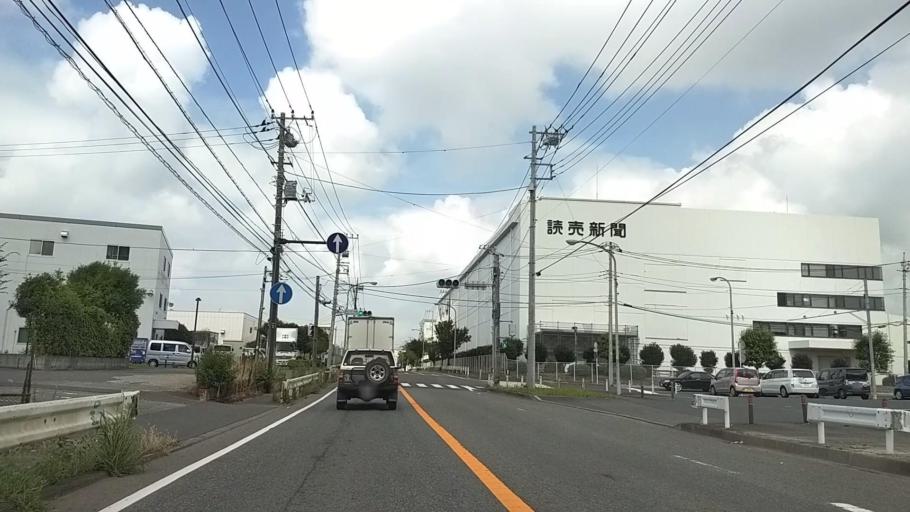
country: JP
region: Kanagawa
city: Minami-rinkan
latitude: 35.4980
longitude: 139.4849
